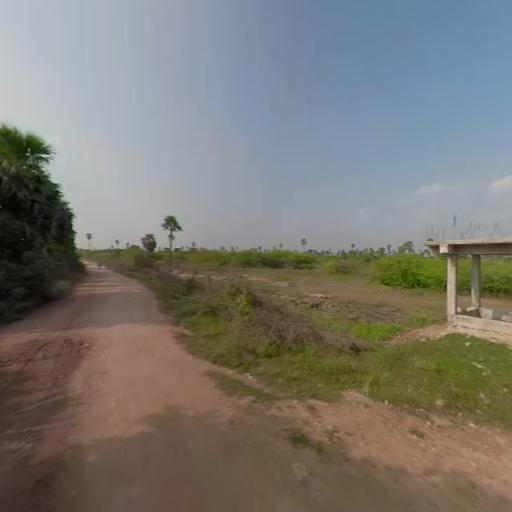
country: IN
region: Telangana
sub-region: Nalgonda
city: Suriapet
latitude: 17.2009
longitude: 79.4878
